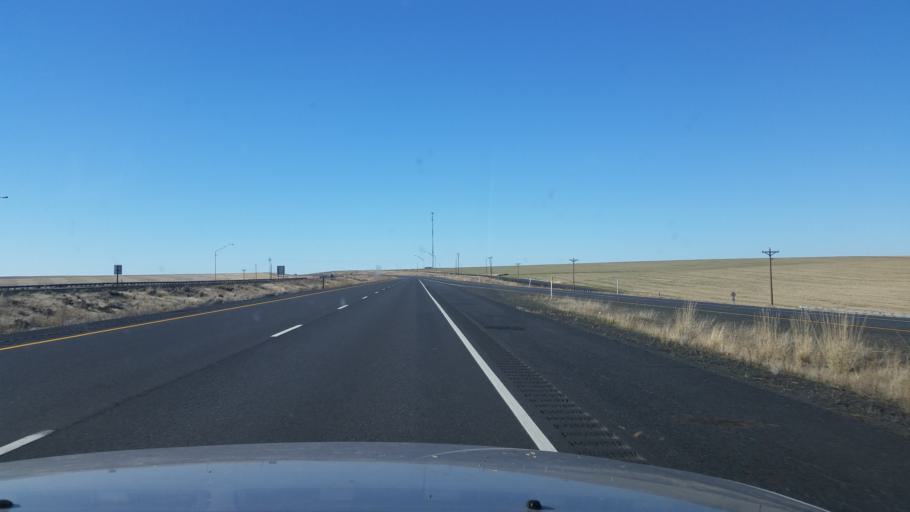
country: US
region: Washington
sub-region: Adams County
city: Ritzville
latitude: 47.0974
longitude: -118.6713
